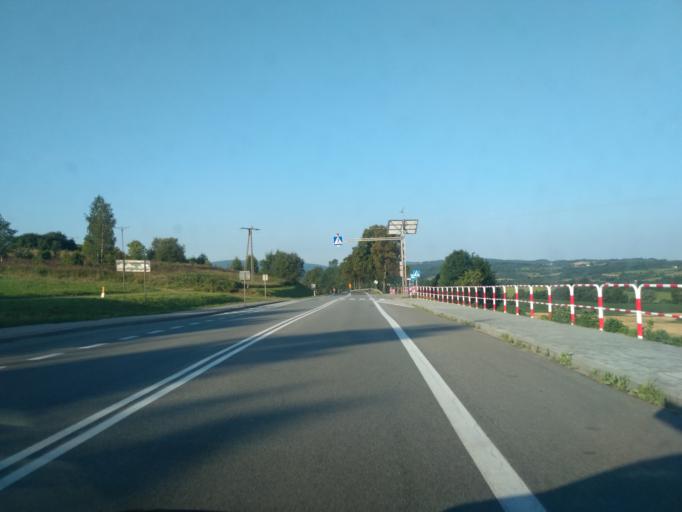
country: PL
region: Subcarpathian Voivodeship
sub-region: Powiat krosnienski
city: Dukla
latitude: 49.6044
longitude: 21.7277
